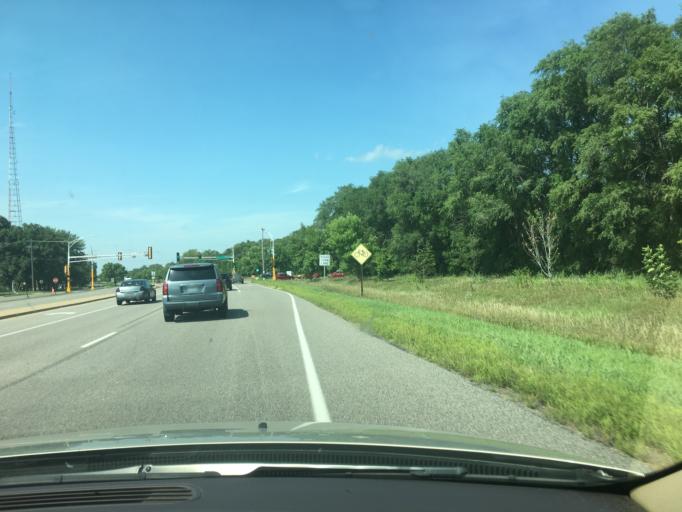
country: US
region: Minnesota
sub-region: Stearns County
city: Saint Cloud
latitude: 45.5357
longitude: -94.1650
